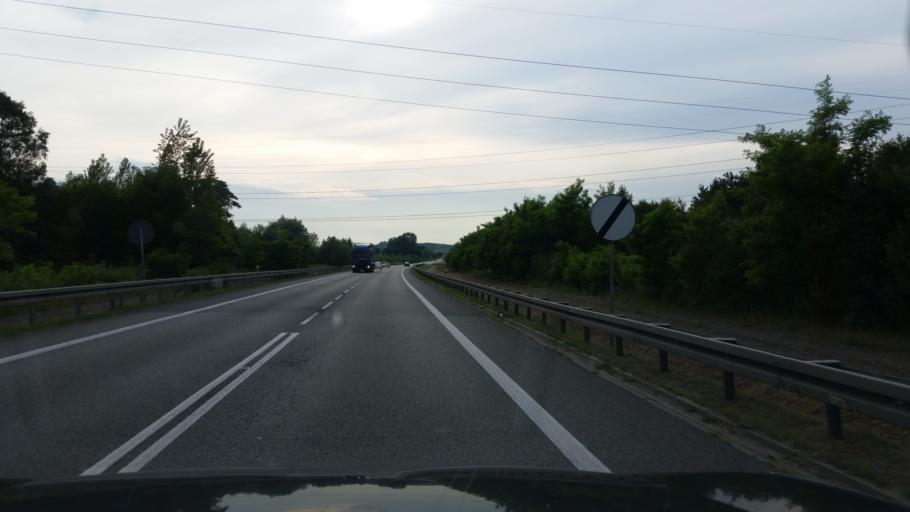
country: PL
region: Silesian Voivodeship
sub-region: Powiat bedzinski
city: Siewierz
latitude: 50.4210
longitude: 19.1917
